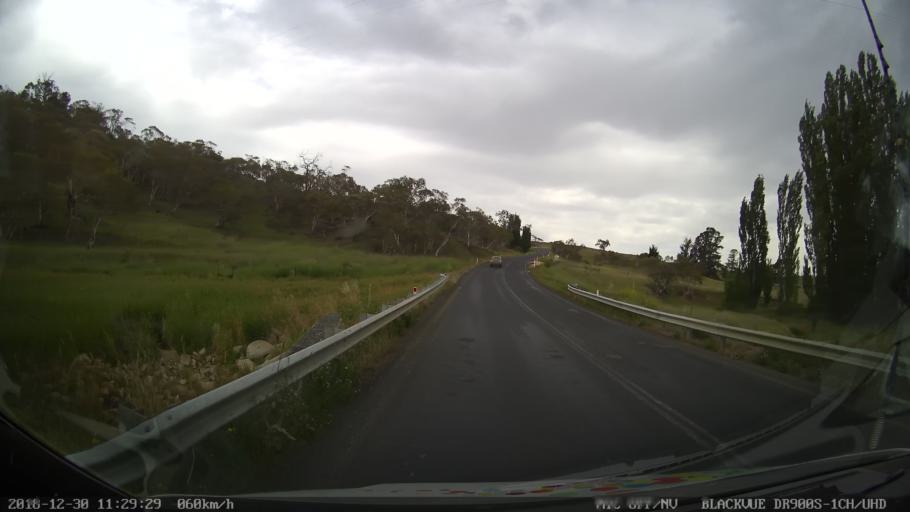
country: AU
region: New South Wales
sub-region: Snowy River
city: Jindabyne
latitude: -36.4502
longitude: 148.6099
